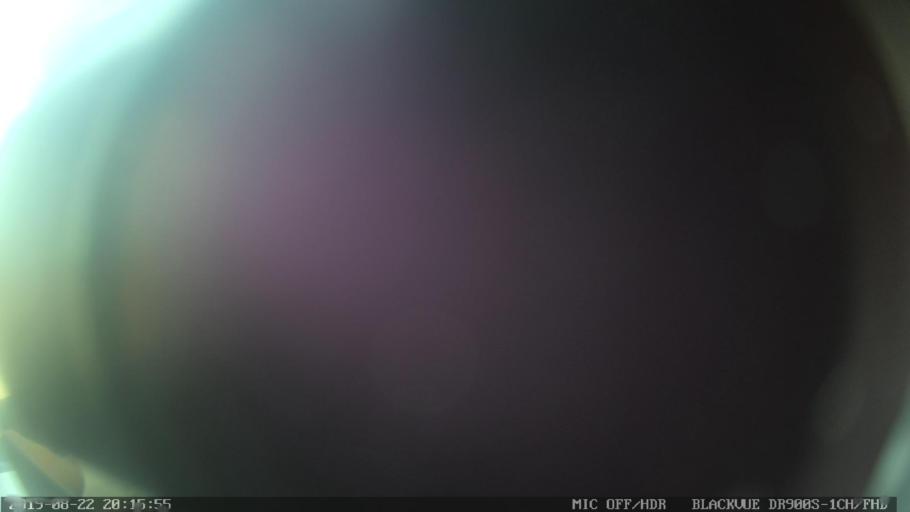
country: PT
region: Guarda
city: Alcains
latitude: 39.9240
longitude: -7.4466
